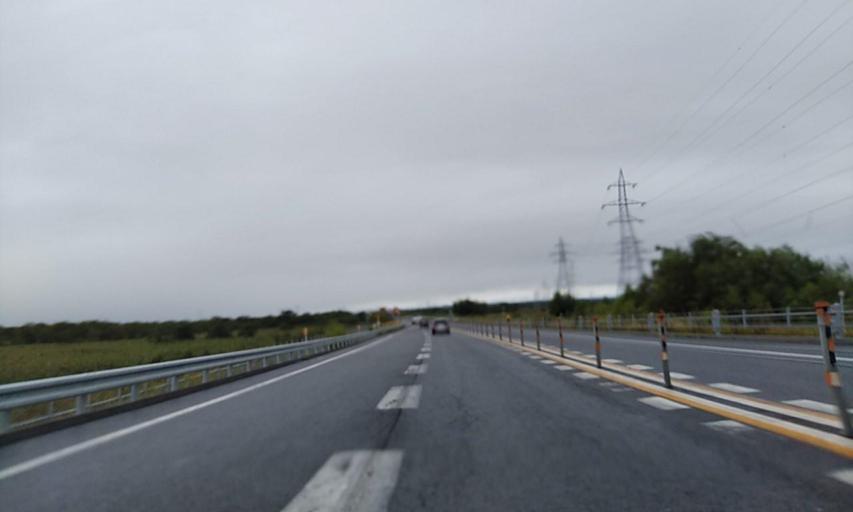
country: JP
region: Hokkaido
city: Kushiro
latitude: 43.0306
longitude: 144.4001
